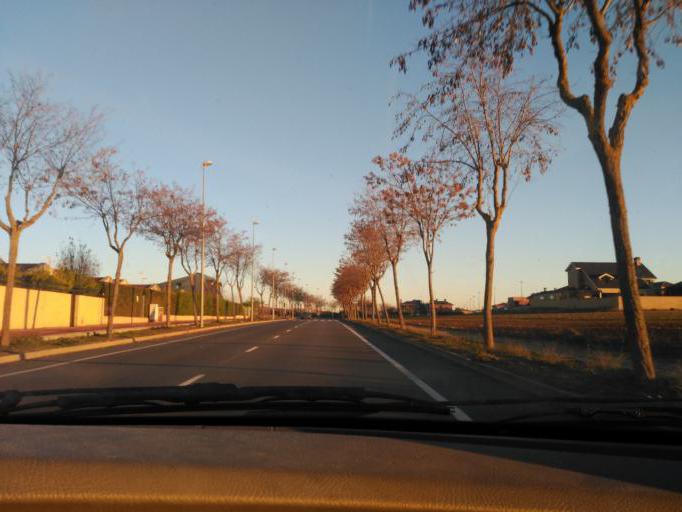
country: ES
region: Castille and Leon
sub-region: Provincia de Salamanca
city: Santa Marta de Tormes
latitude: 40.9363
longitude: -5.6341
